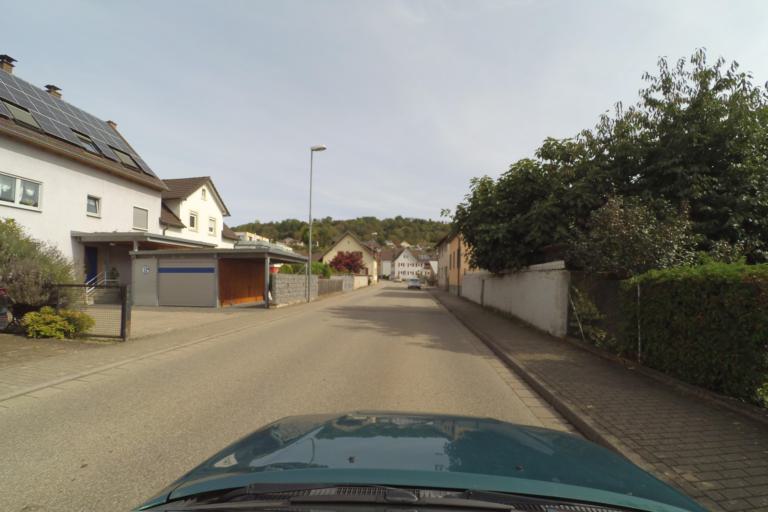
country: DE
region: Baden-Wuerttemberg
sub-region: Freiburg Region
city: Herbolzheim
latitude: 48.2238
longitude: 7.7755
